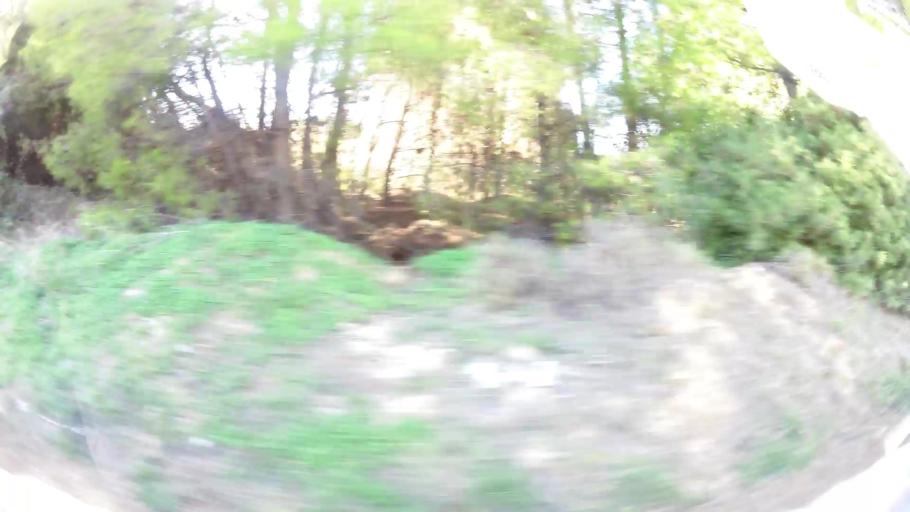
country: GR
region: Attica
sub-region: Nomarchia Anatolikis Attikis
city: Dioni
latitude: 38.0160
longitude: 23.9291
